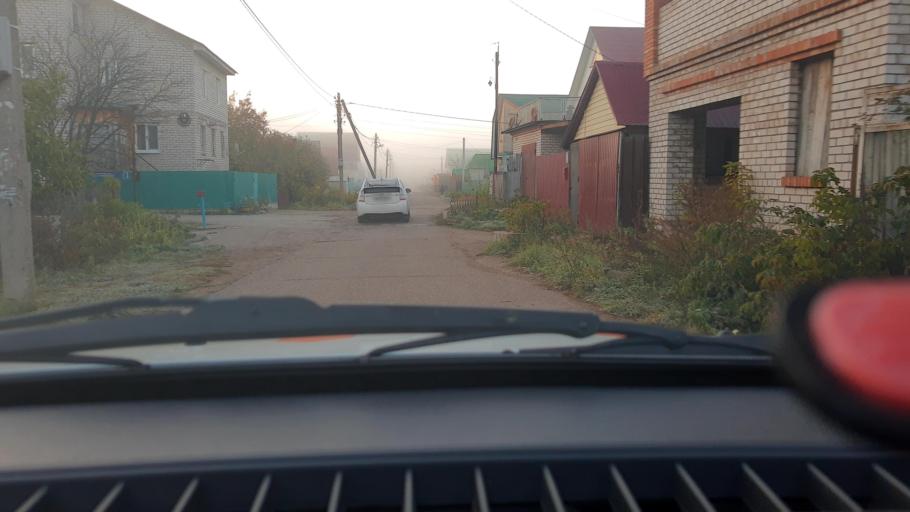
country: RU
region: Bashkortostan
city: Ufa
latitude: 54.7314
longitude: 55.9037
